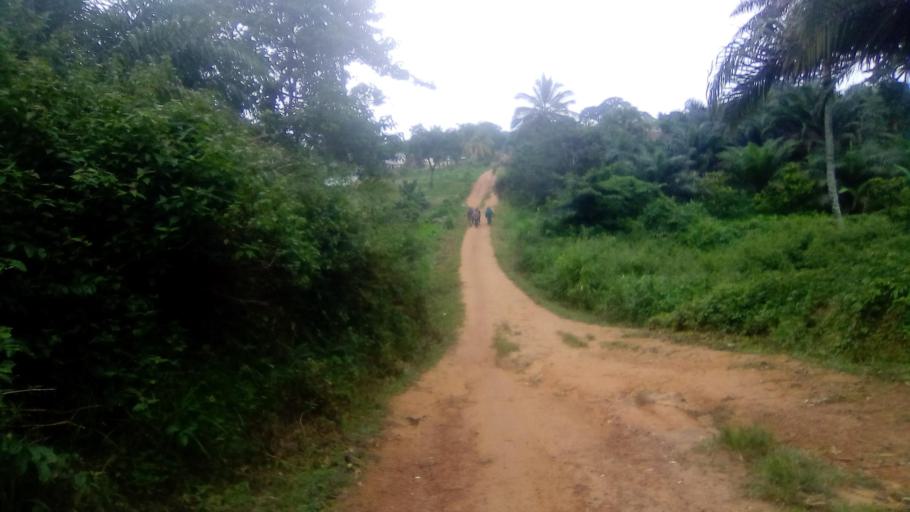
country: SL
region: Eastern Province
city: Kailahun
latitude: 8.2953
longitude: -10.6051
